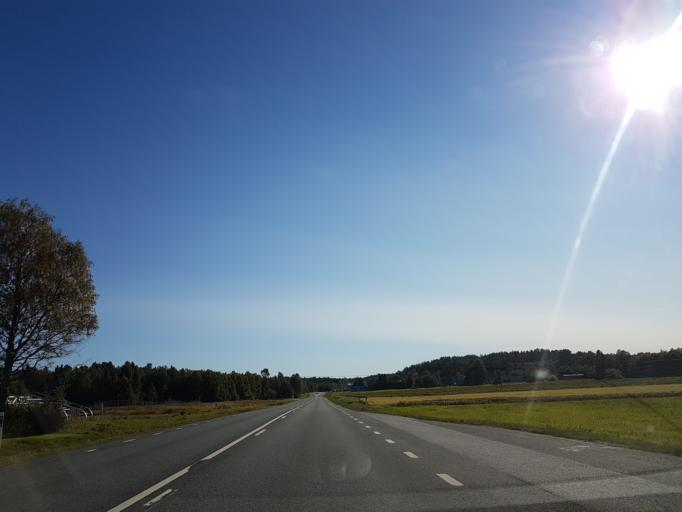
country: SE
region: Vaesterbotten
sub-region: Skelleftea Kommun
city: Burea
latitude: 64.3779
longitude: 21.3041
